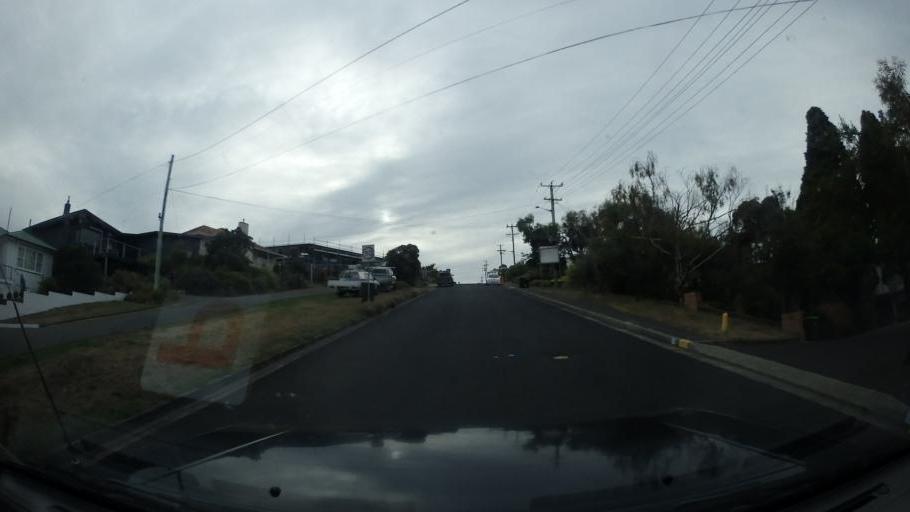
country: AU
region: Tasmania
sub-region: Clarence
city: Bellerive
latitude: -42.8699
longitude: 147.3740
